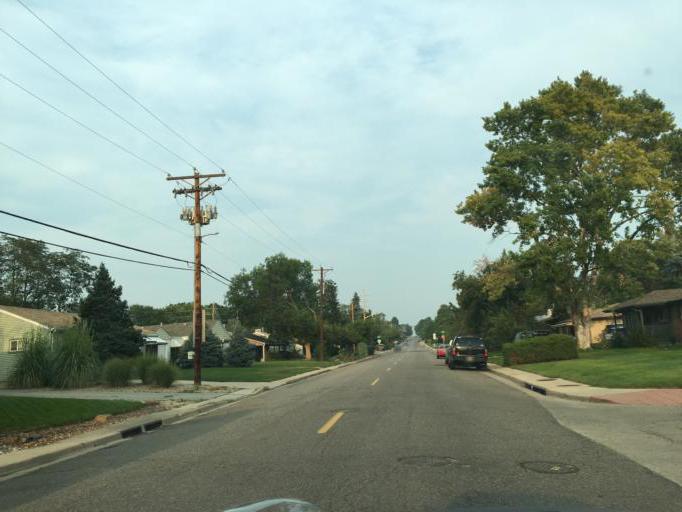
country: US
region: Colorado
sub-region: Arapahoe County
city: Glendale
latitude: 39.6821
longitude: -104.9332
